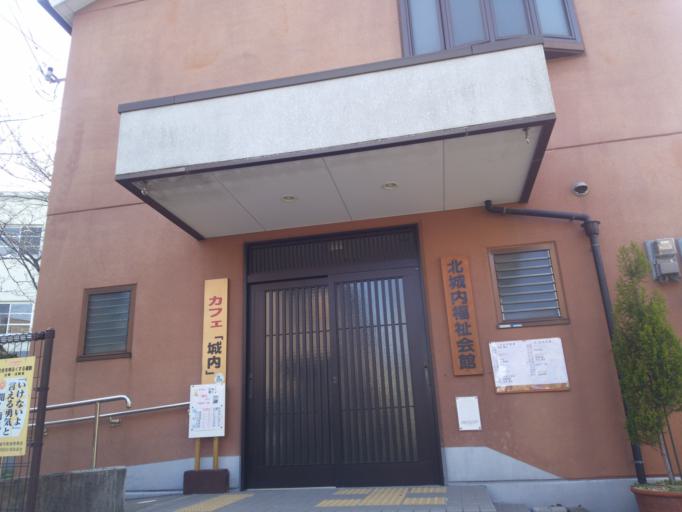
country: JP
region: Hyogo
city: Amagasaki
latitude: 34.7164
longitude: 135.4198
